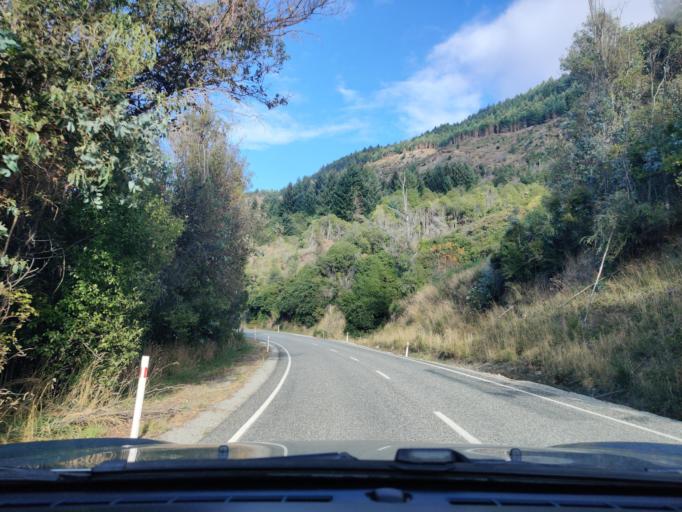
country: NZ
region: Otago
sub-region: Queenstown-Lakes District
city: Queenstown
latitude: -45.0473
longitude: 168.6235
